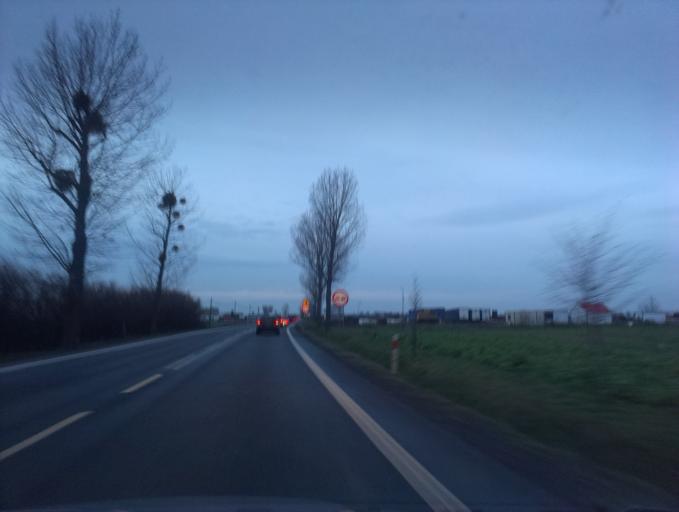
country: PL
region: Greater Poland Voivodeship
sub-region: Powiat obornicki
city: Oborniki
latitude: 52.5858
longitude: 16.8271
